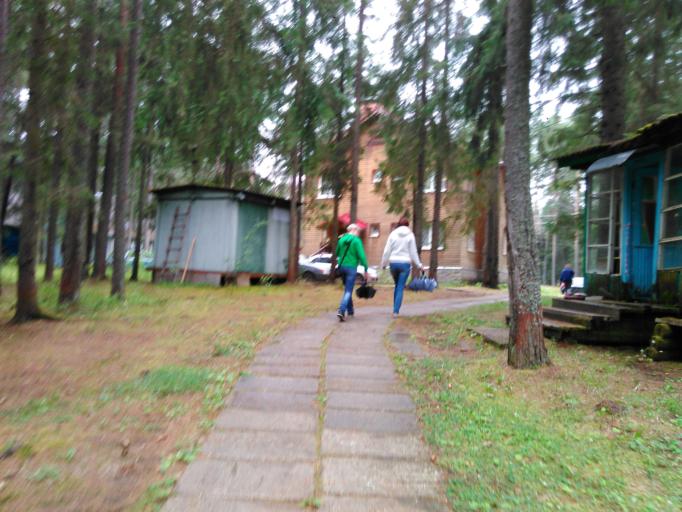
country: RU
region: Tverskaya
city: Ostashkov
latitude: 57.2051
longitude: 32.9808
